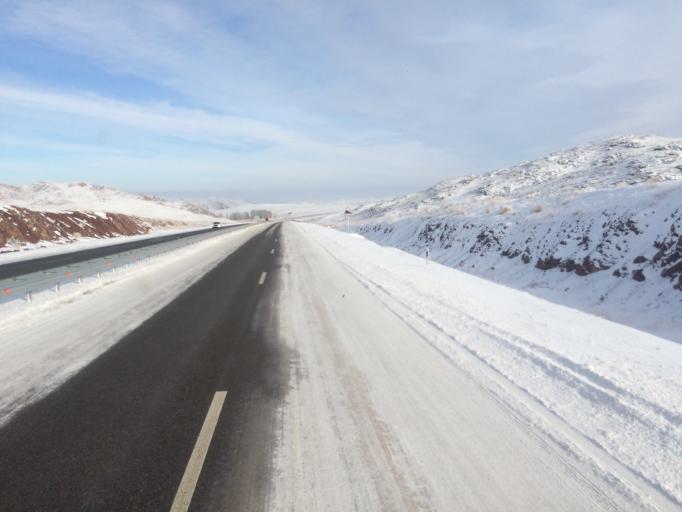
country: KZ
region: Zhambyl
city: Georgiyevka
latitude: 43.4314
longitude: 74.9124
